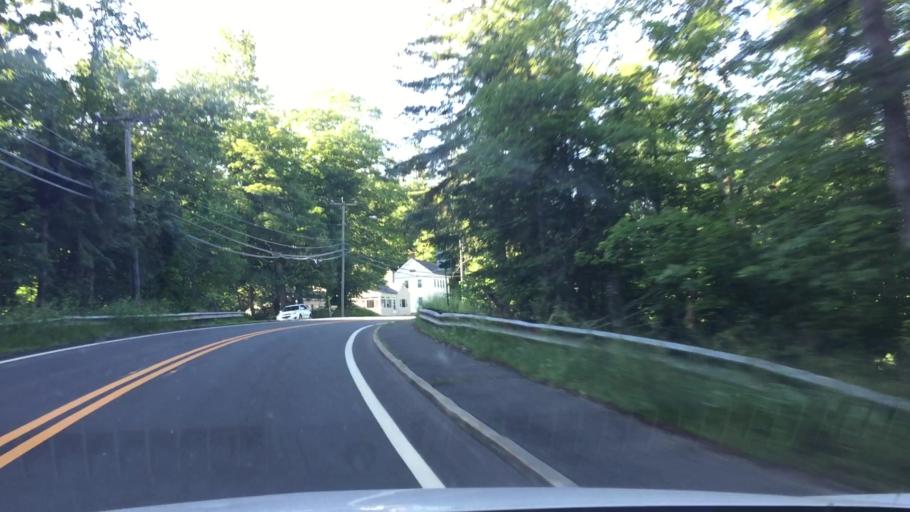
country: US
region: Massachusetts
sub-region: Berkshire County
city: Becket
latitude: 42.3288
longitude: -73.0835
